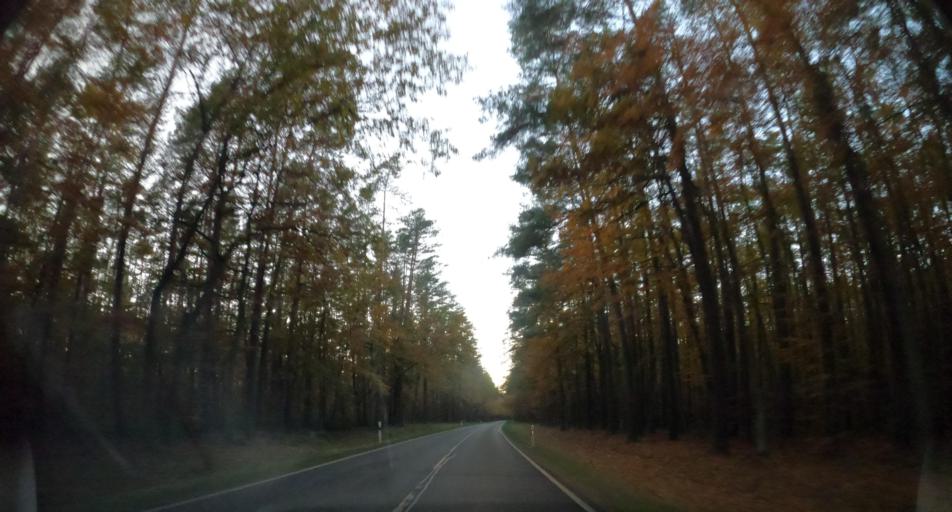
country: DE
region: Mecklenburg-Vorpommern
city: Usedom
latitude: 53.7668
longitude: 13.9340
